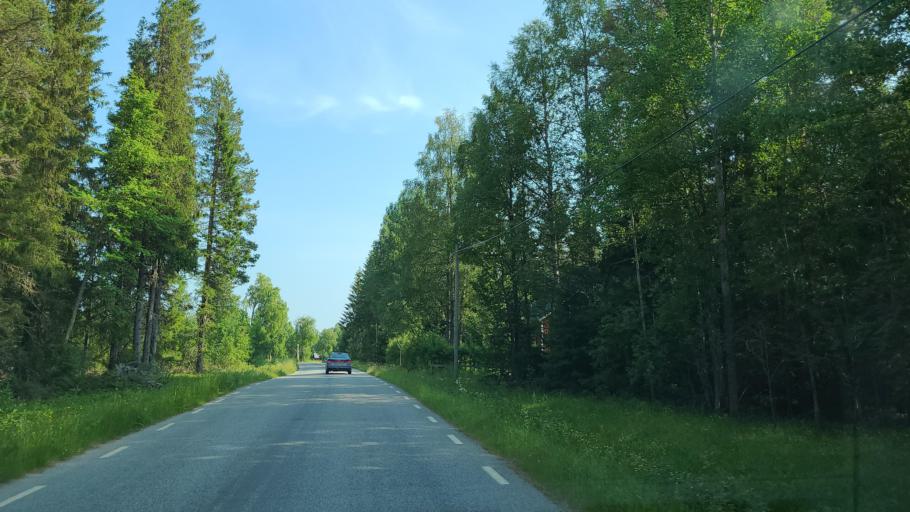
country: SE
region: Vaesterbotten
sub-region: Skelleftea Kommun
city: Burea
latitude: 64.3504
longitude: 21.3358
